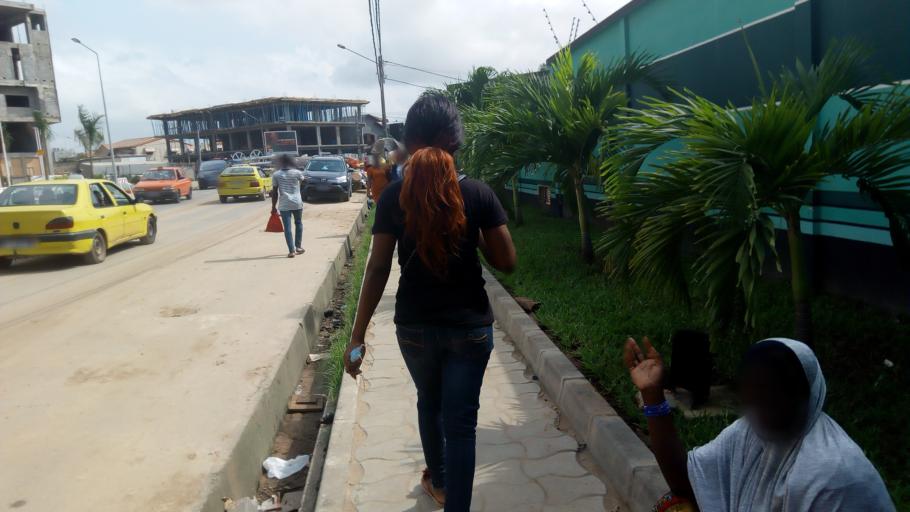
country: CI
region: Lagunes
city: Abobo
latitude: 5.3656
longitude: -3.9603
